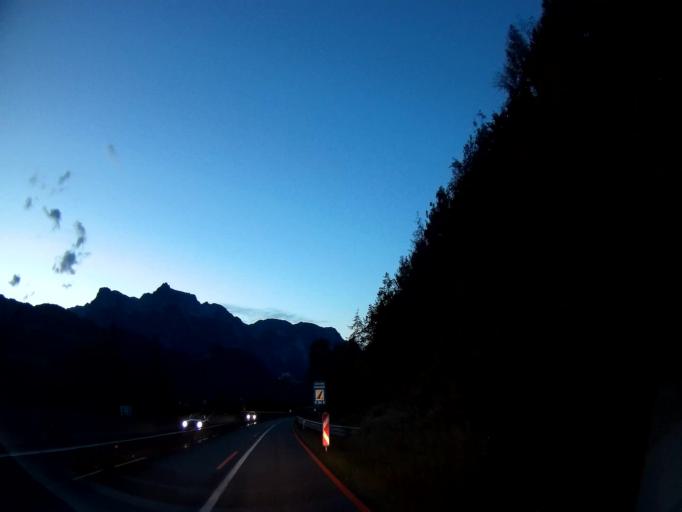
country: AT
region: Salzburg
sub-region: Politischer Bezirk Sankt Johann im Pongau
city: Pfarrwerfen
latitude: 47.4615
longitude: 13.2068
